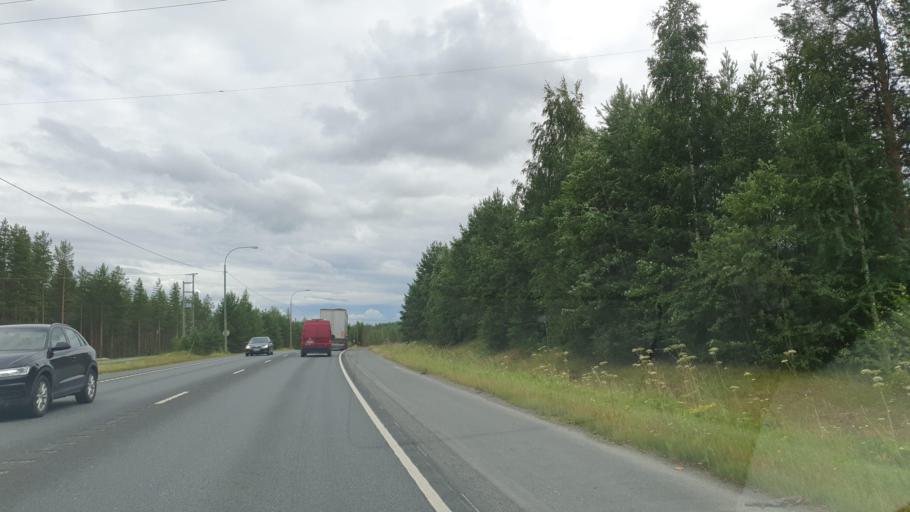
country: FI
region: Northern Savo
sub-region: Ylae-Savo
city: Iisalmi
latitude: 63.4884
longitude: 27.2852
